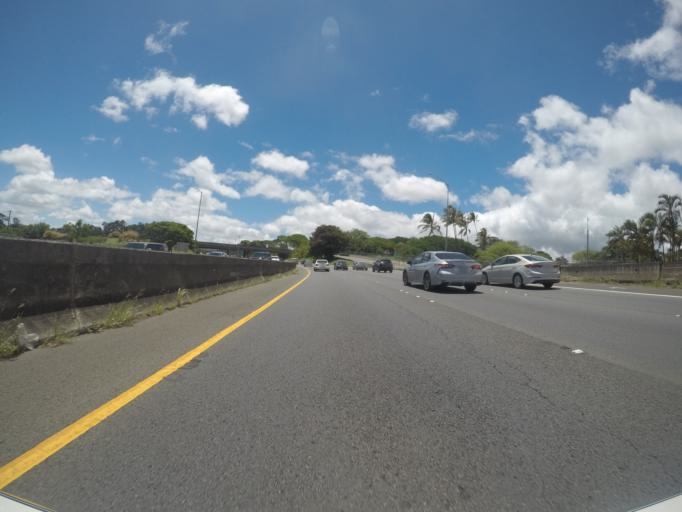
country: US
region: Hawaii
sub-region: Honolulu County
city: Honolulu
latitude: 21.3417
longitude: -157.8865
